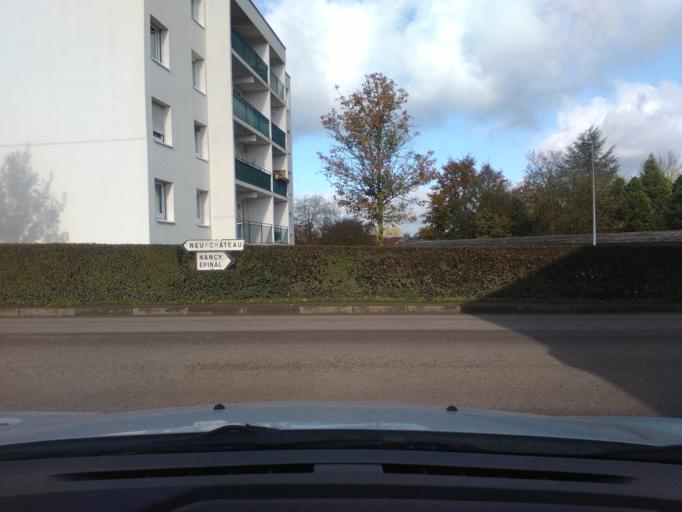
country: FR
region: Lorraine
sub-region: Departement des Vosges
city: Mirecourt
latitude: 48.3077
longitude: 6.1311
